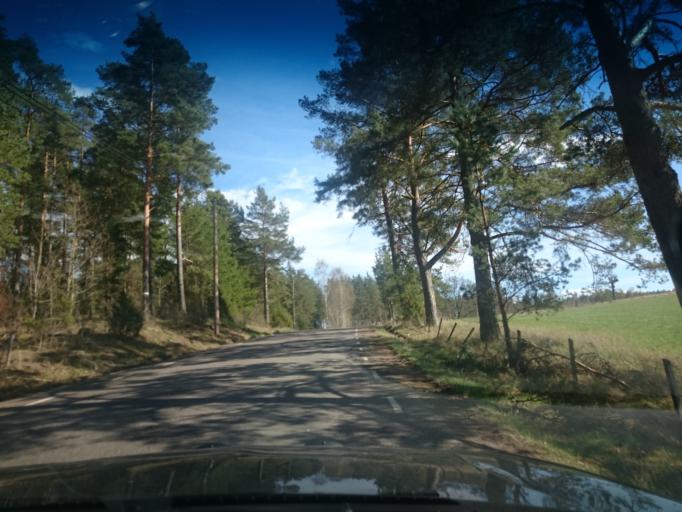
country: SE
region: Kalmar
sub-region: Hultsfreds Kommun
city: Virserum
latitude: 57.3434
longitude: 15.5584
